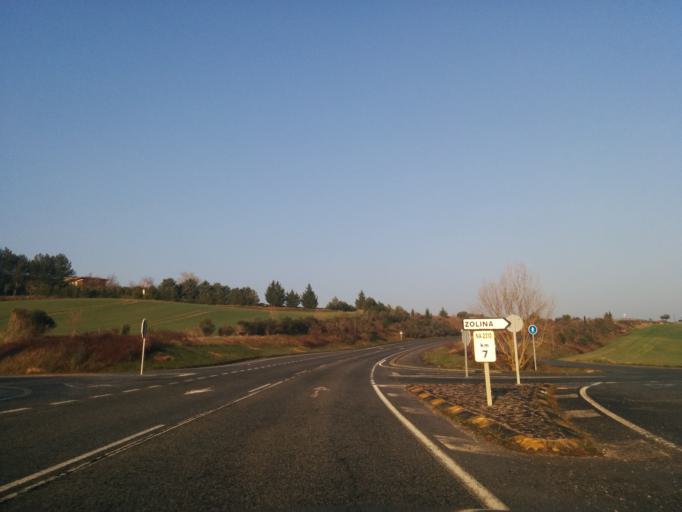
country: ES
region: Navarre
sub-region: Provincia de Navarra
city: Elorz
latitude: 42.7645
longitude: -1.5788
